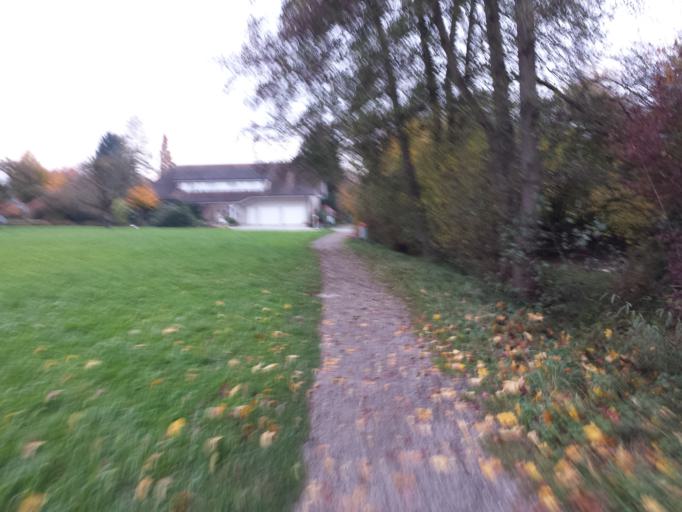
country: CH
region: Thurgau
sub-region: Arbon District
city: Salmsach
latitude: 47.5709
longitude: 9.3641
